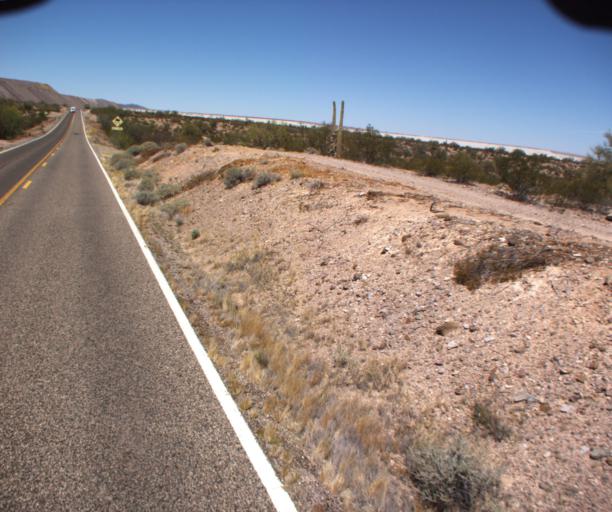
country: US
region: Arizona
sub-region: Pima County
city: Ajo
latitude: 32.3497
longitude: -112.8162
